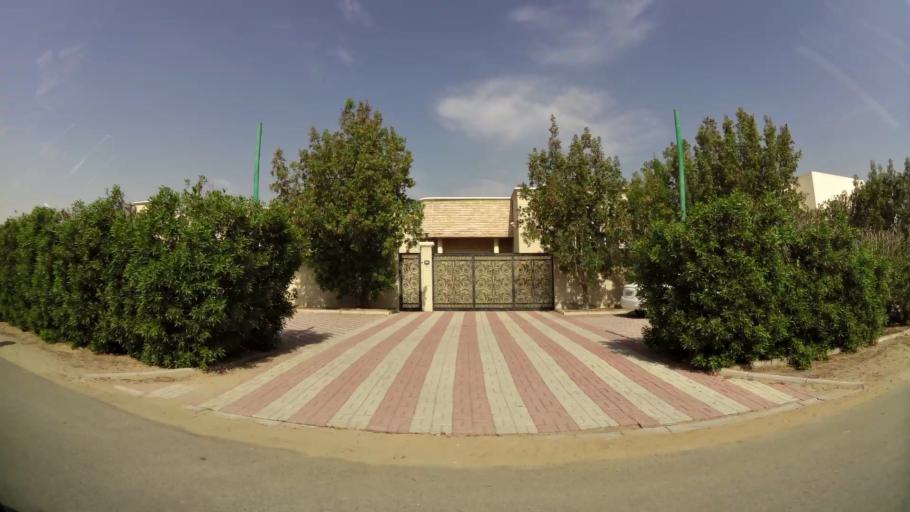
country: AE
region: Ash Shariqah
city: Sharjah
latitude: 25.2483
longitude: 55.4310
